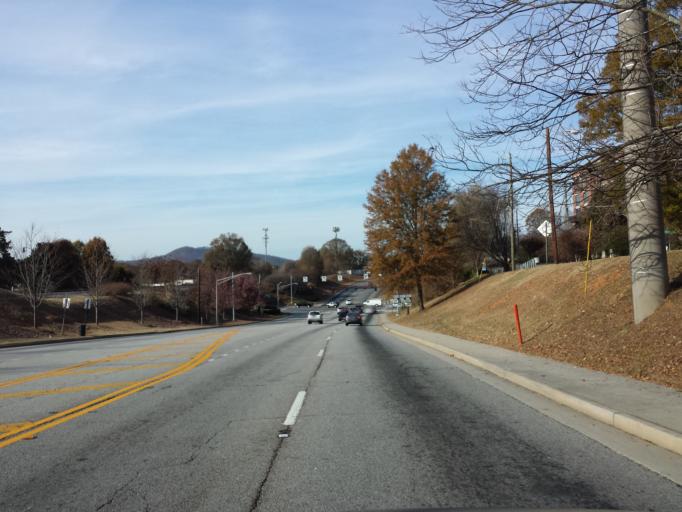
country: US
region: Georgia
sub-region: Cobb County
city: Marietta
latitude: 33.9462
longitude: -84.5476
